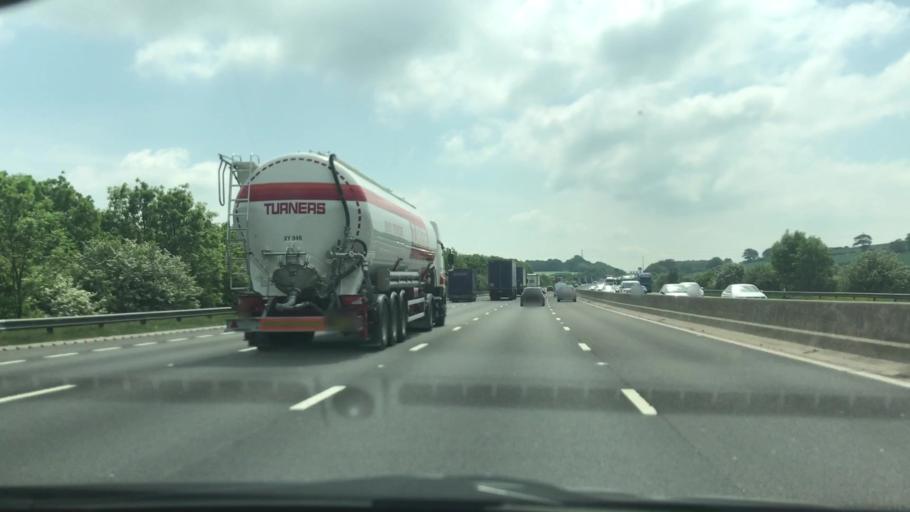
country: GB
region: England
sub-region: Derbyshire
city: Tibshelf
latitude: 53.1630
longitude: -1.3243
